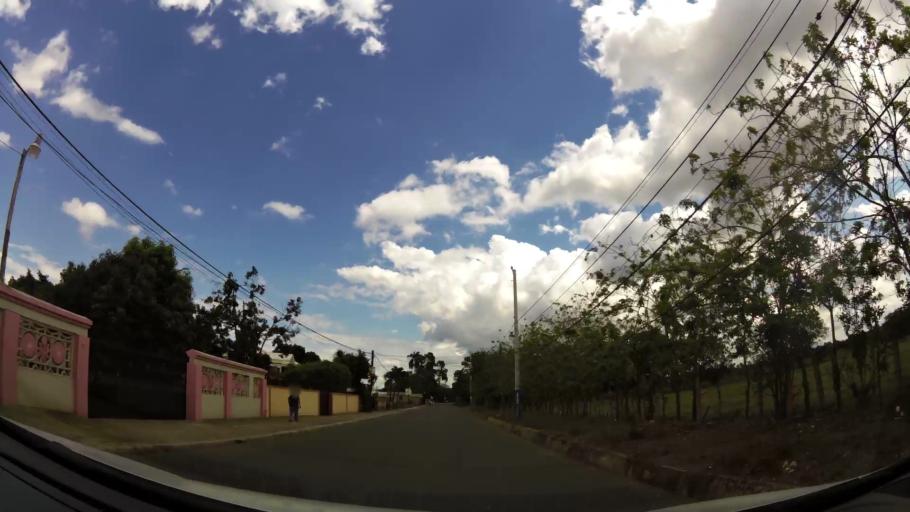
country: DO
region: Santiago
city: Licey al Medio
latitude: 19.3945
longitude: -70.6454
